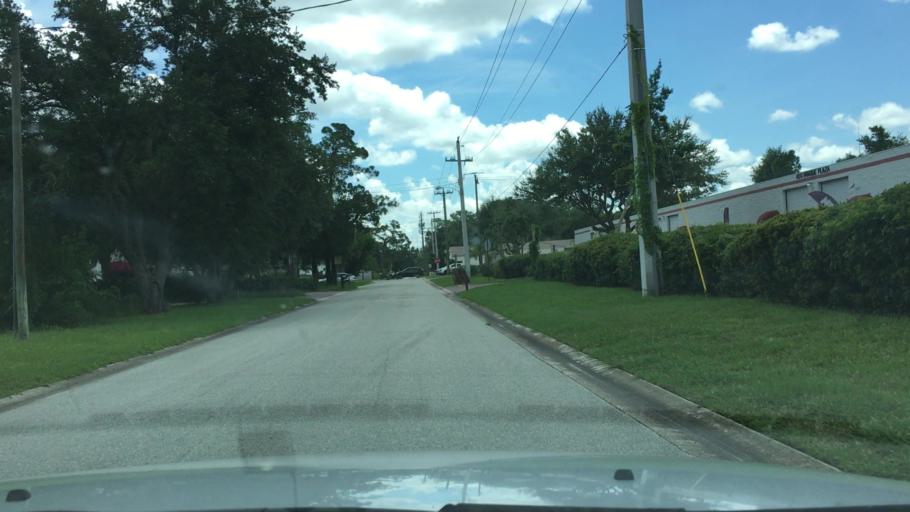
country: US
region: Florida
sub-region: Volusia County
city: Ormond Beach
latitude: 29.2723
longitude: -81.0584
